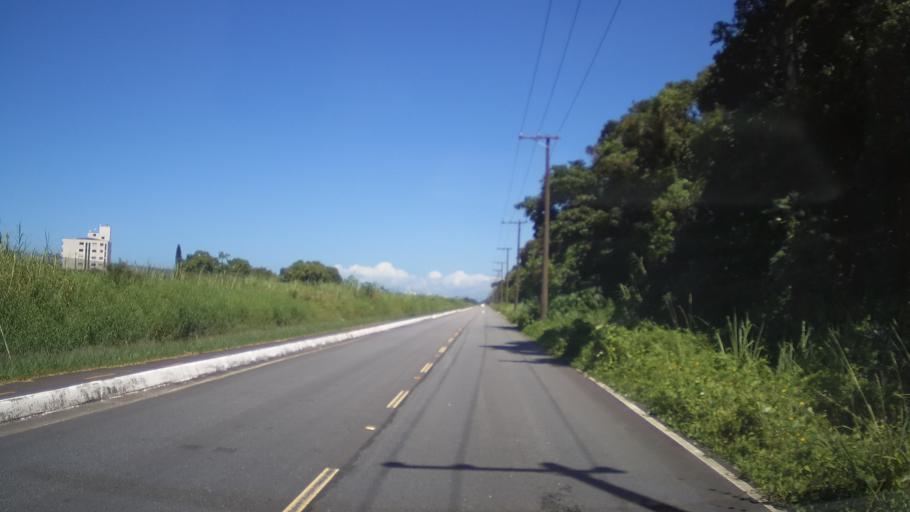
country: BR
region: Sao Paulo
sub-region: Mongagua
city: Mongagua
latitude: -24.0668
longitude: -46.5727
